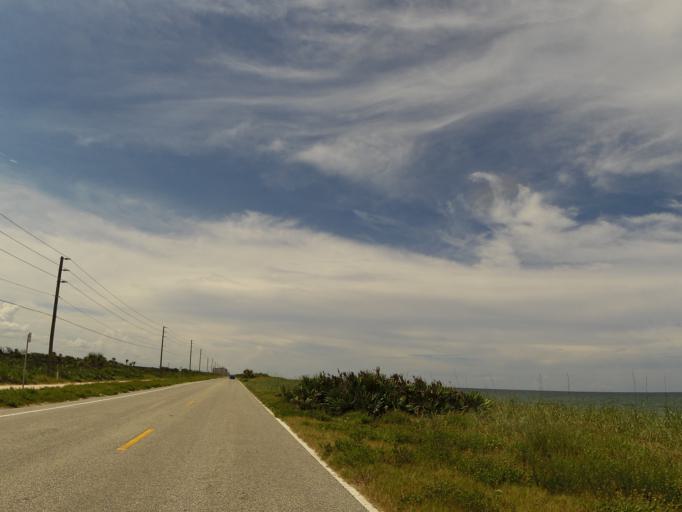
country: US
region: Florida
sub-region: Flagler County
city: Flagler Beach
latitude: 29.4131
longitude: -81.0963
